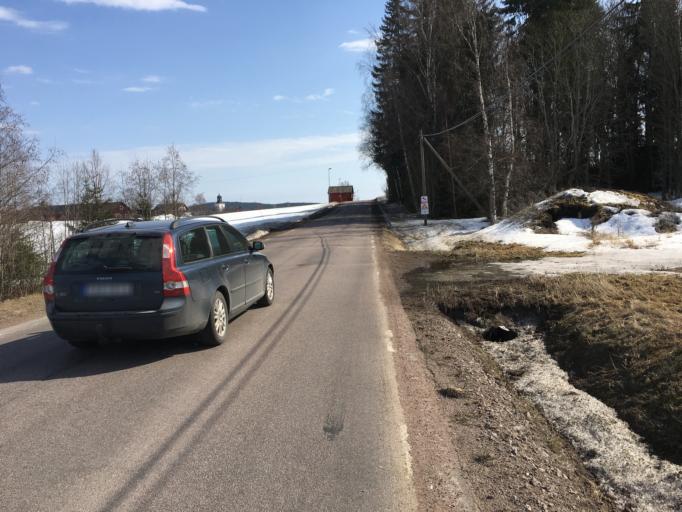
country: SE
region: Gaevleborg
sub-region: Hofors Kommun
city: Hofors
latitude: 60.5136
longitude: 16.4559
